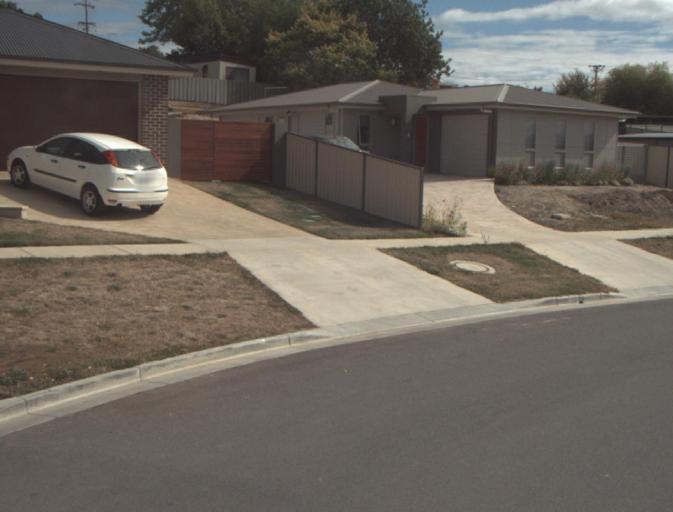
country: AU
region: Tasmania
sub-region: Launceston
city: Summerhill
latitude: -41.4657
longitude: 147.1350
